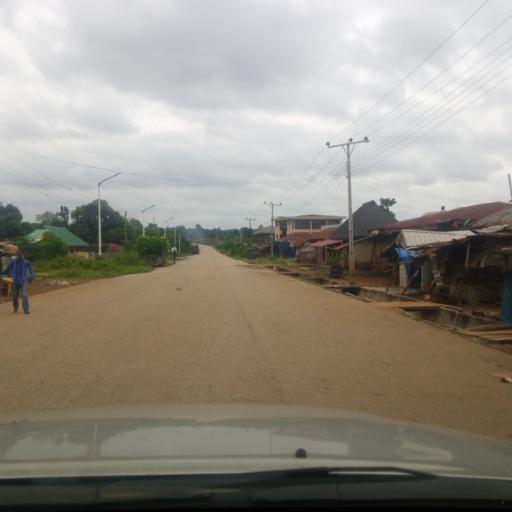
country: NG
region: Ebonyi
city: Effium
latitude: 6.6313
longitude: 8.0591
